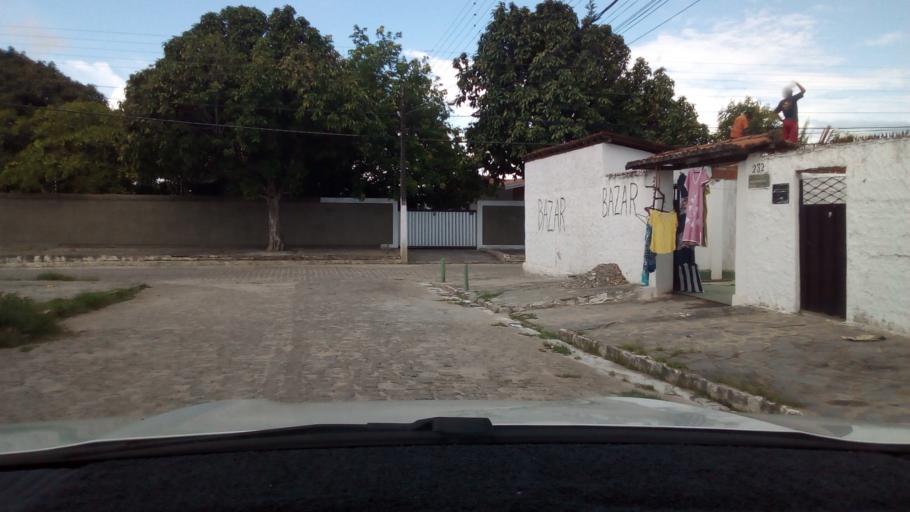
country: BR
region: Paraiba
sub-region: Joao Pessoa
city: Joao Pessoa
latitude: -7.1659
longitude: -34.8546
